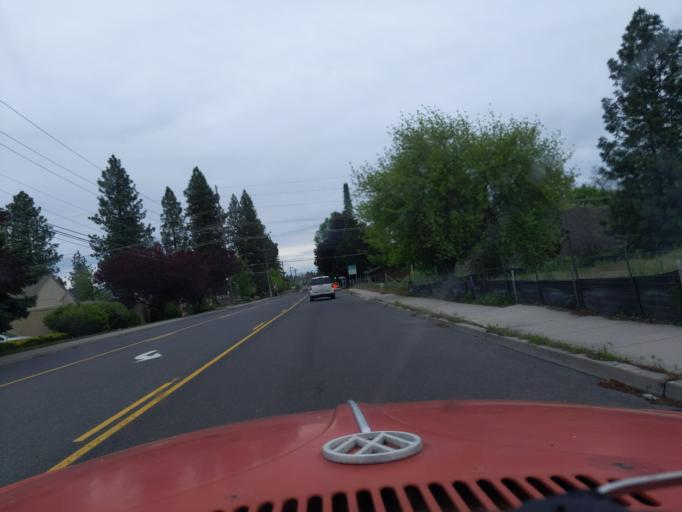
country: US
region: Washington
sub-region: Spokane County
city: Spokane
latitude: 47.6050
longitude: -117.3684
